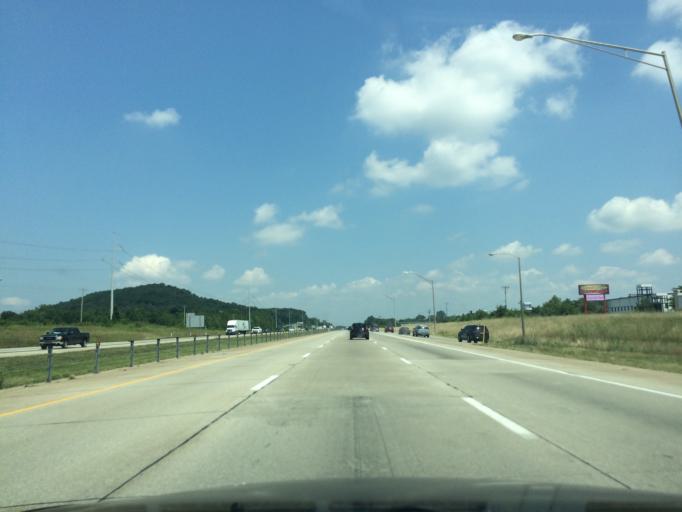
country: US
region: Kentucky
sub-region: Bullitt County
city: Brooks
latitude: 38.0660
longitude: -85.6993
